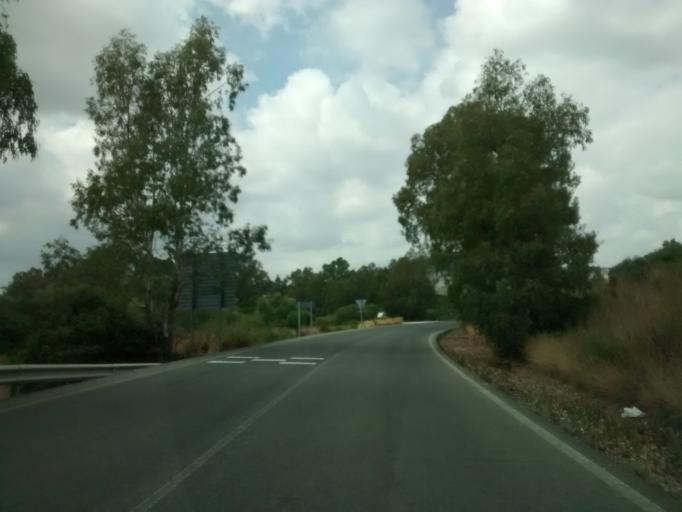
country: ES
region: Andalusia
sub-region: Provincia de Cadiz
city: Medina Sidonia
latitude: 36.4556
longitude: -5.8906
